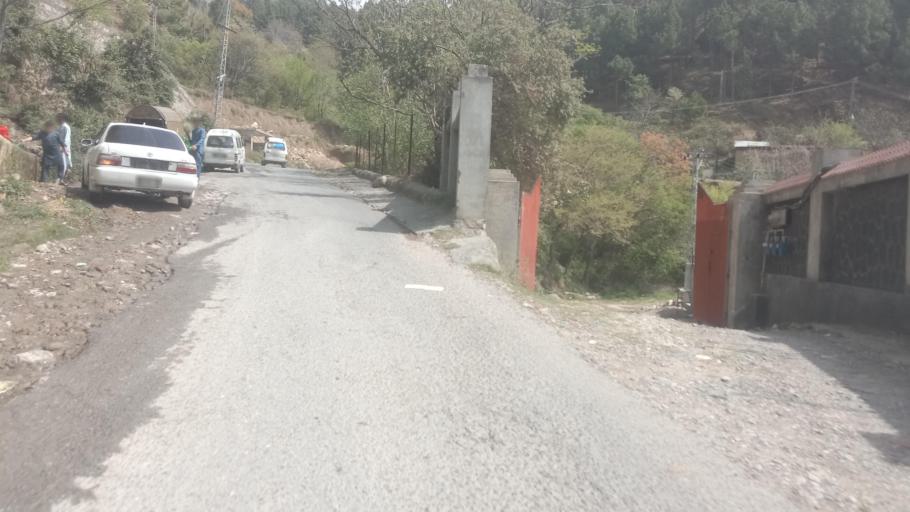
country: PK
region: Khyber Pakhtunkhwa
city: Abbottabad
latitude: 34.1678
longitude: 73.2829
